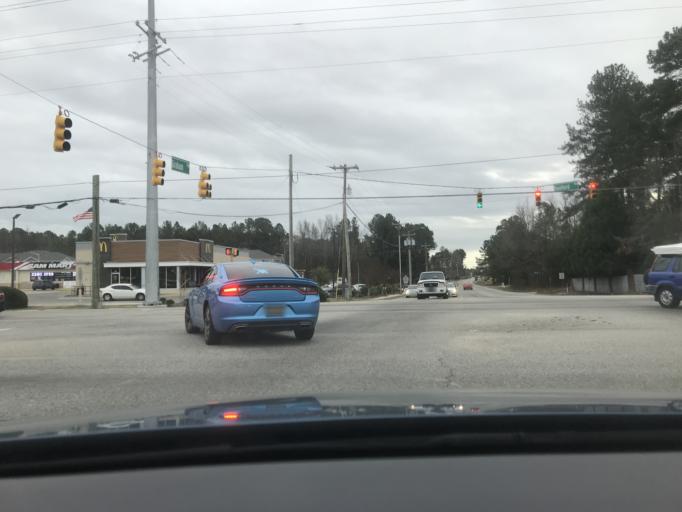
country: US
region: North Carolina
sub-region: Hoke County
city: Rockfish
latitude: 35.0377
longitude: -79.0074
